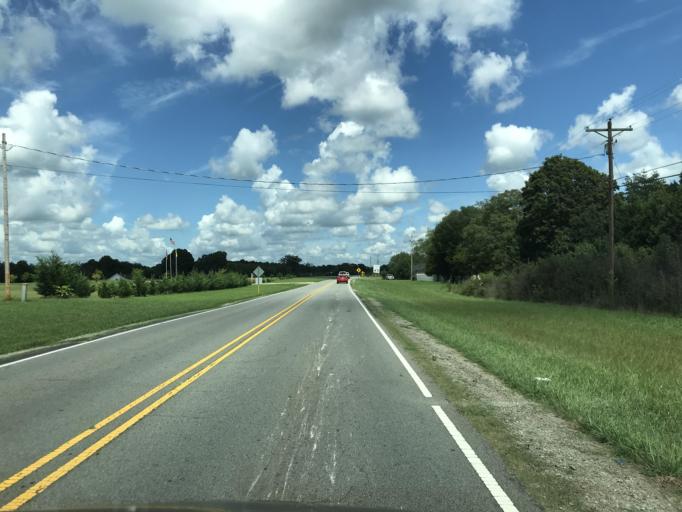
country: US
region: North Carolina
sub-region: Lincoln County
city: Lincolnton
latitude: 35.5030
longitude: -81.2072
